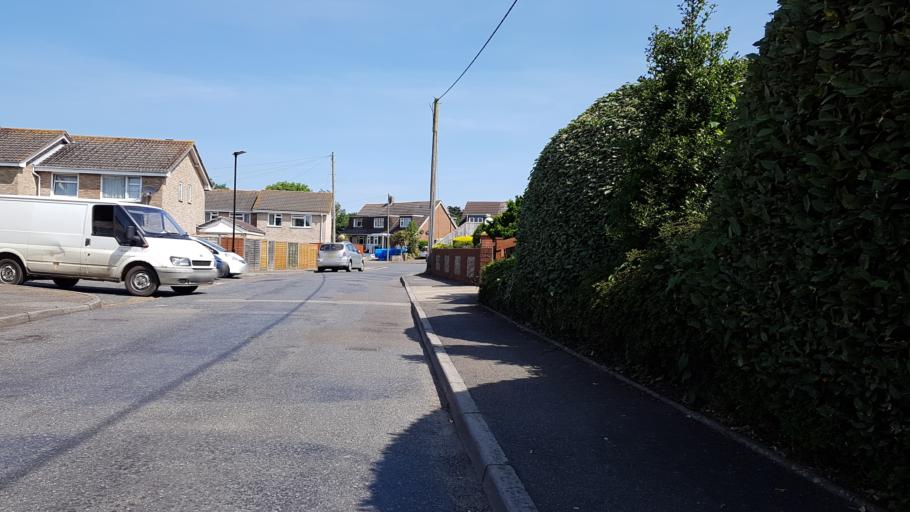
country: GB
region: England
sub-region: Isle of Wight
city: Northwood
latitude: 50.7506
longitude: -1.3121
